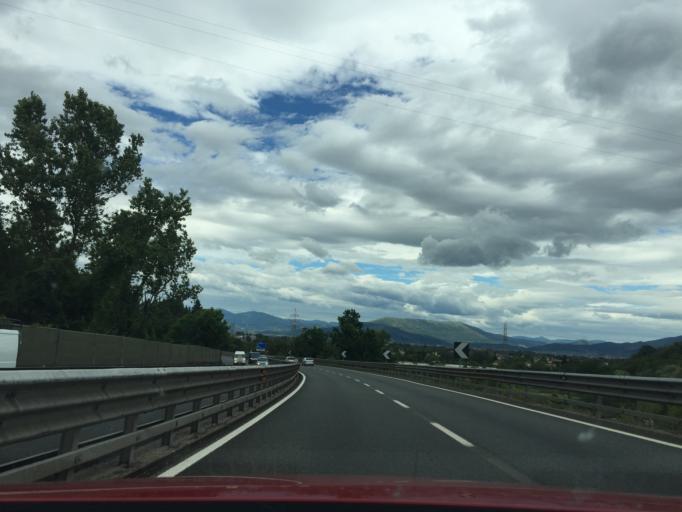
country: IT
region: Tuscany
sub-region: Province of Florence
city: Lastra a Signa
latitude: 43.7603
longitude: 11.1278
